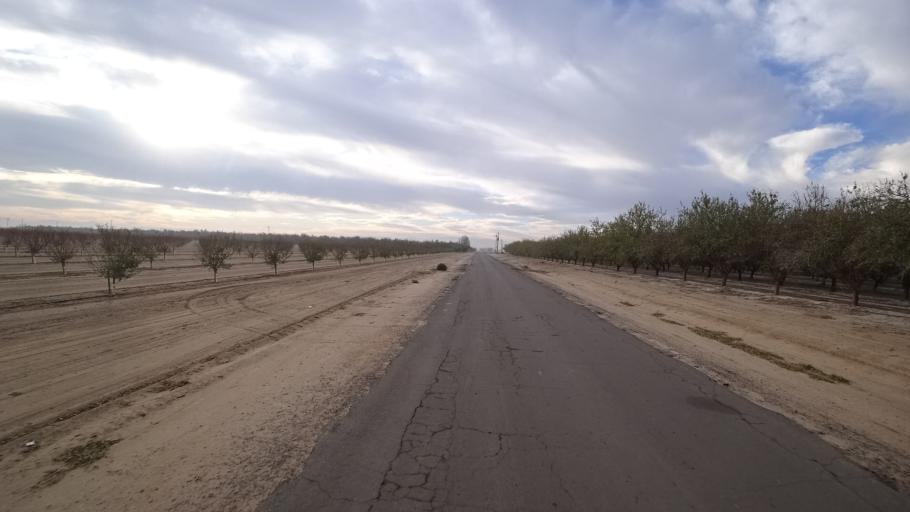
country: US
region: California
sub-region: Kern County
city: Rosedale
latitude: 35.4069
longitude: -119.1898
